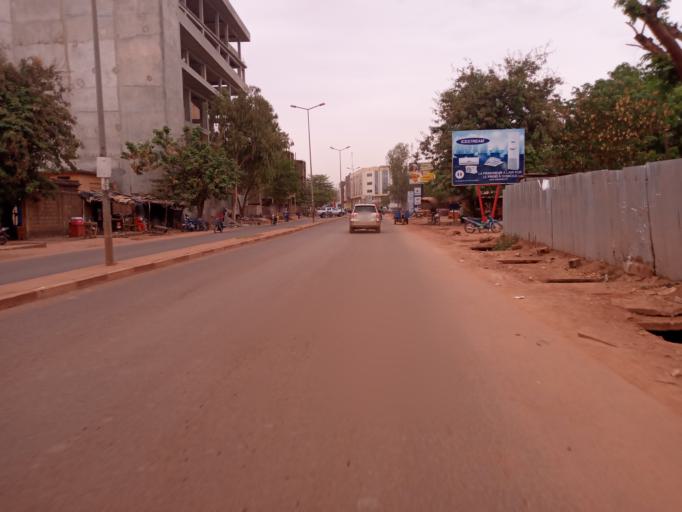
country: ML
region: Bamako
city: Bamako
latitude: 12.6355
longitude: -8.0246
